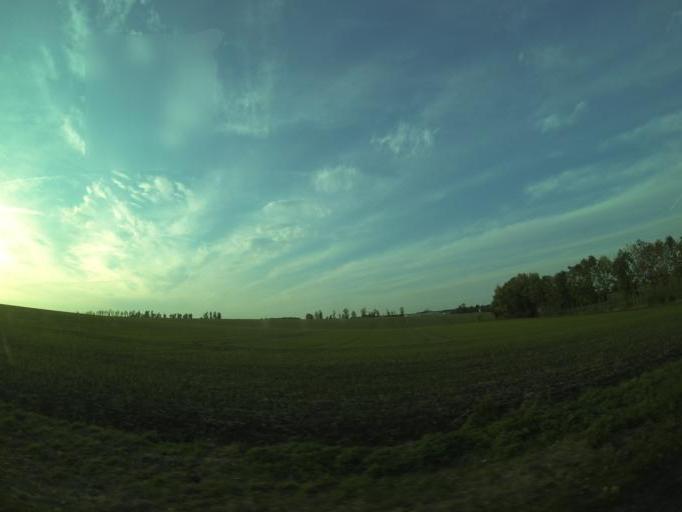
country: DE
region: Thuringia
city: Drogen
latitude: 50.9224
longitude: 12.3235
